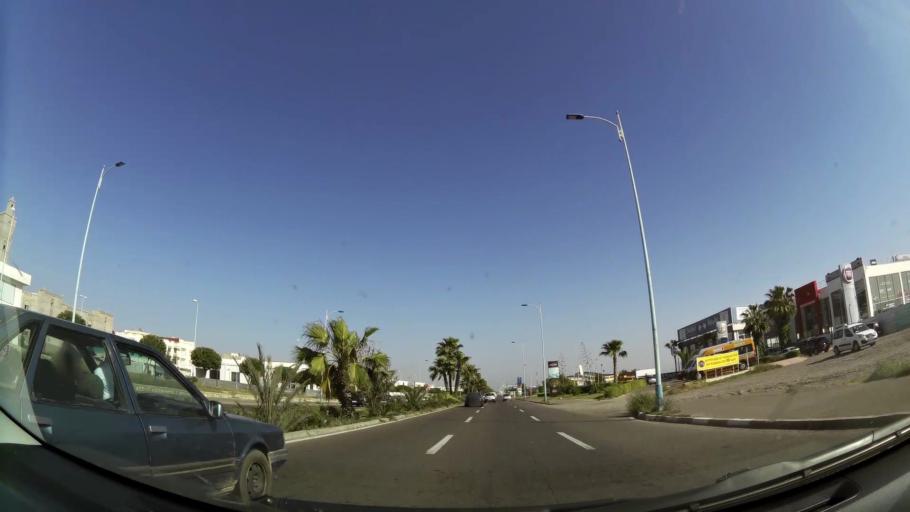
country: MA
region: Oued ed Dahab-Lagouira
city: Dakhla
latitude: 30.3948
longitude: -9.5203
